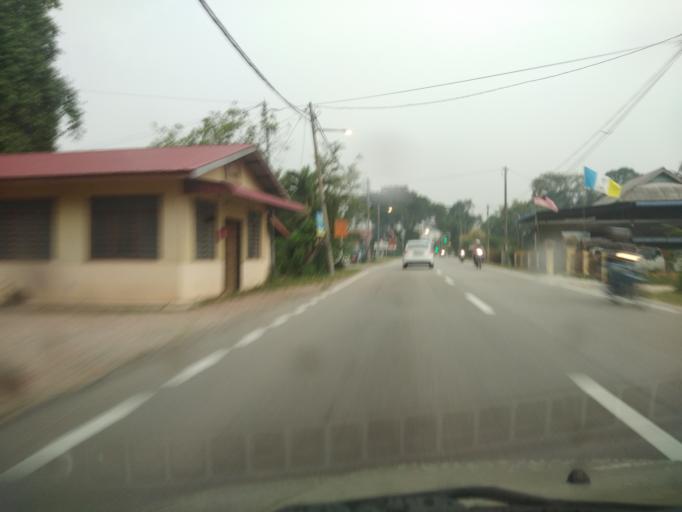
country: MY
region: Penang
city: Permatang Kuching
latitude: 5.4802
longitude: 100.4013
